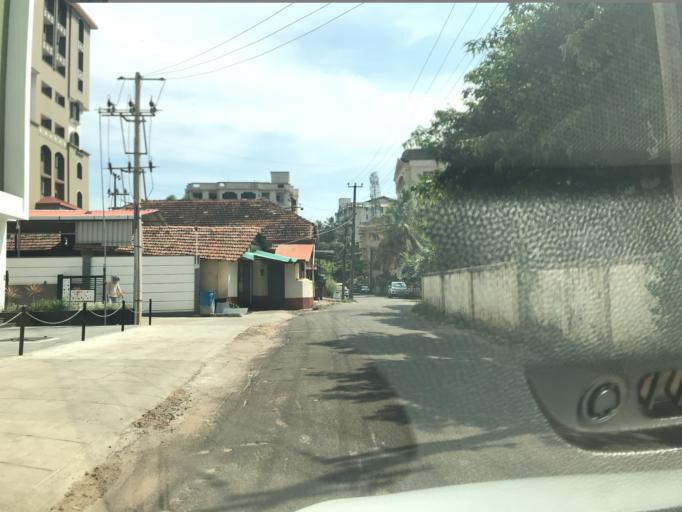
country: IN
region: Karnataka
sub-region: Dakshina Kannada
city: Mangalore
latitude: 12.8774
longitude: 74.8448
